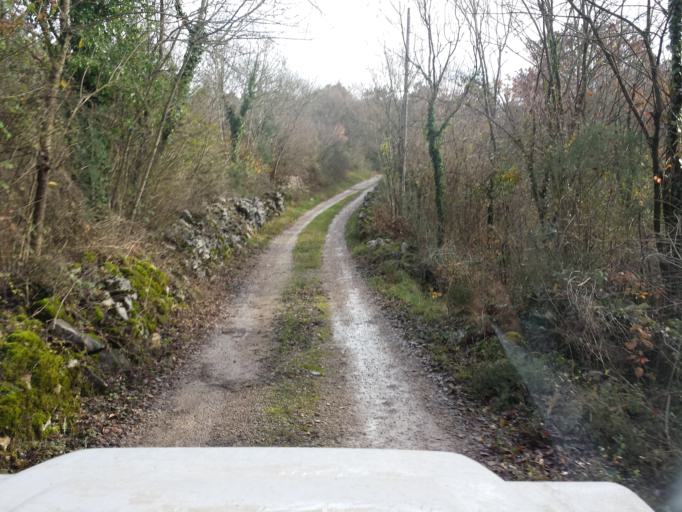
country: IT
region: Friuli Venezia Giulia
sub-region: Provincia di Gorizia
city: Savogna d'Isonzo
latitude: 45.8812
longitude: 13.5656
